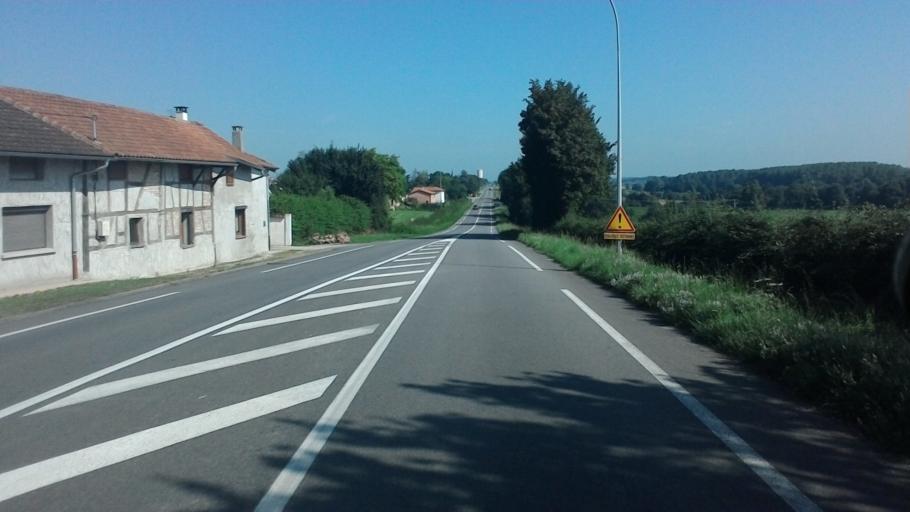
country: FR
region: Rhone-Alpes
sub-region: Departement de l'Ain
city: Montrevel-en-Bresse
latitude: 46.3512
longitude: 5.1250
